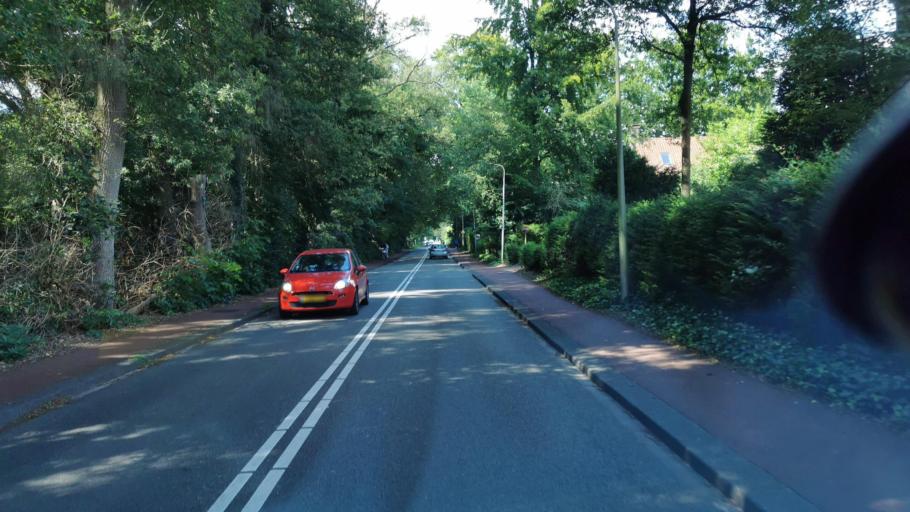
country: NL
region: Overijssel
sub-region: Gemeente Enschede
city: Enschede
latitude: 52.2368
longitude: 6.9190
